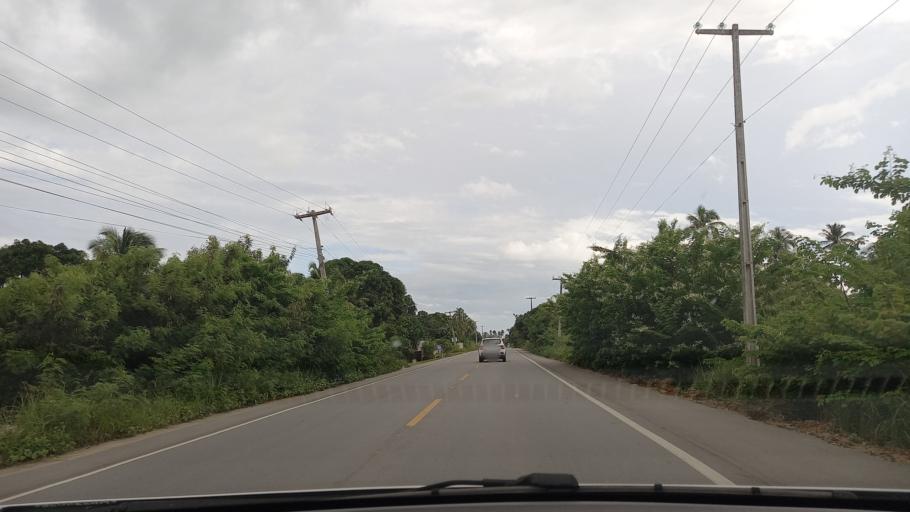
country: BR
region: Alagoas
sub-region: Maragogi
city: Maragogi
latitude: -8.9700
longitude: -35.1827
